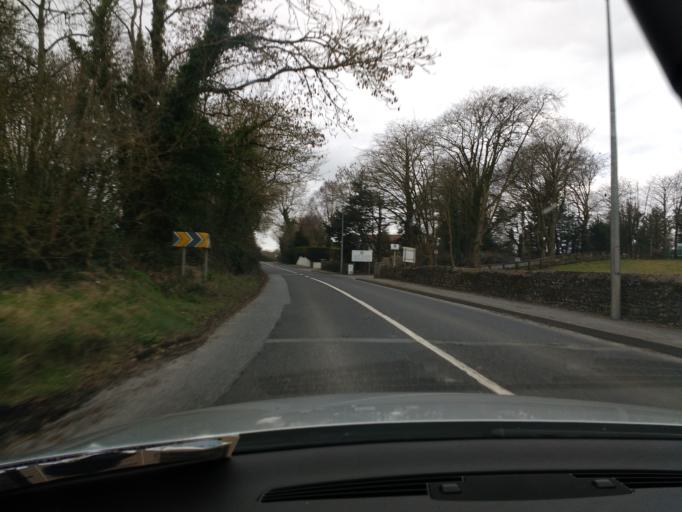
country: IE
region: Leinster
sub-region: Kilkenny
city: Kilkenny
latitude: 52.6750
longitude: -7.2718
